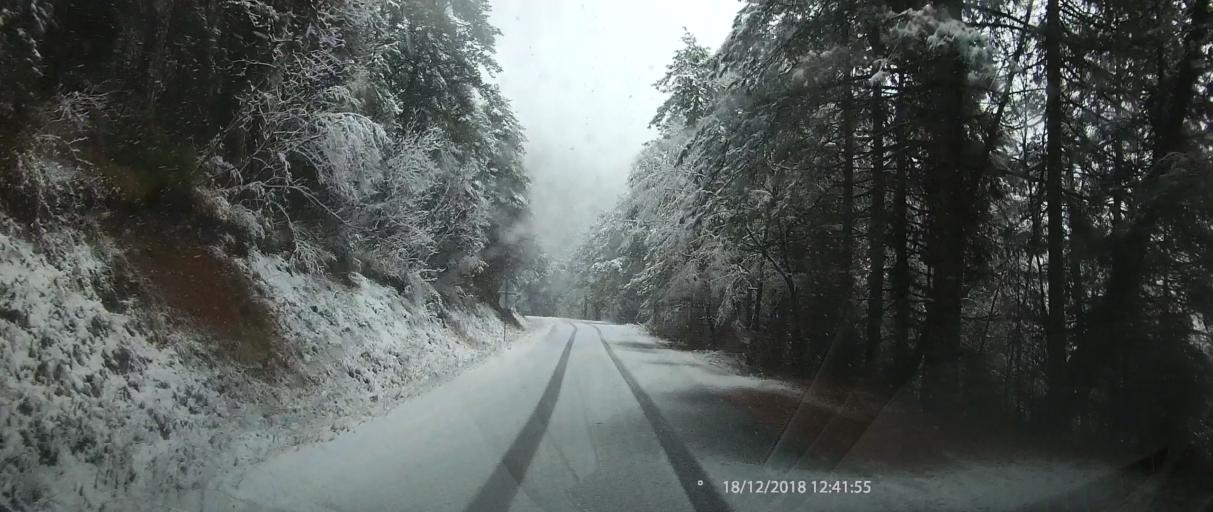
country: GR
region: Central Macedonia
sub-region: Nomos Pierias
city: Litochoro
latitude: 40.0947
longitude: 22.4202
